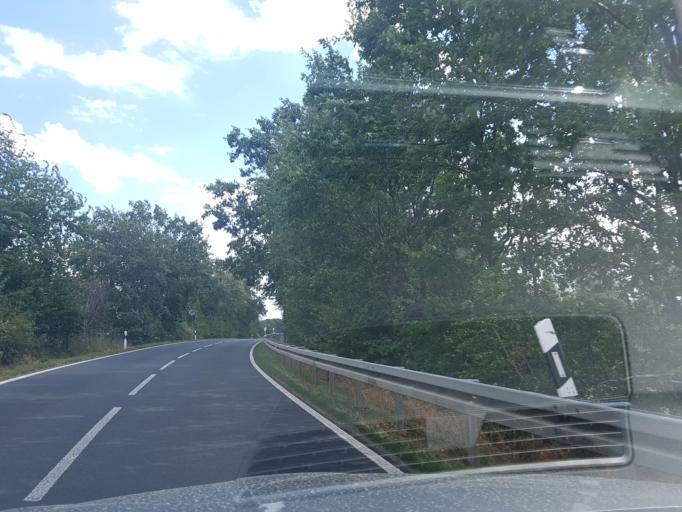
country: DE
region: Saxony
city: Priestewitz
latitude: 51.2608
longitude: 13.5459
